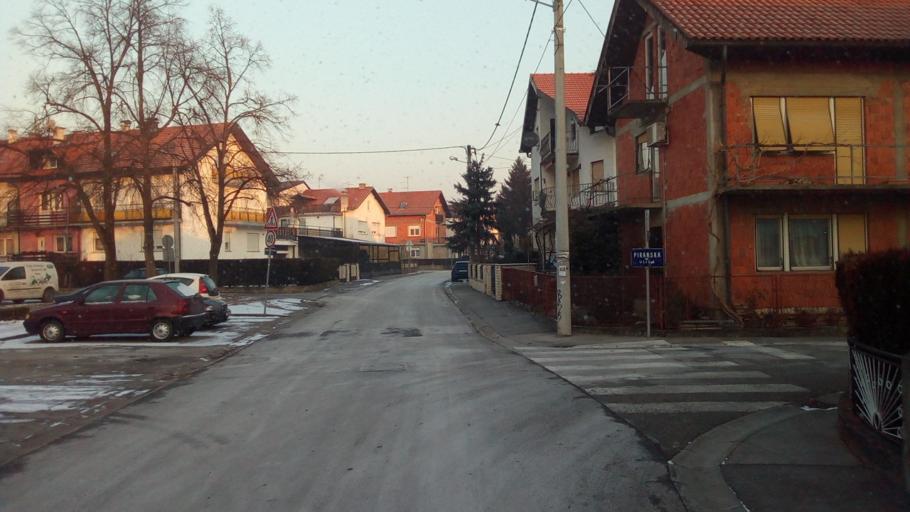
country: HR
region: Grad Zagreb
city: Dubrava
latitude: 45.8105
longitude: 16.0480
